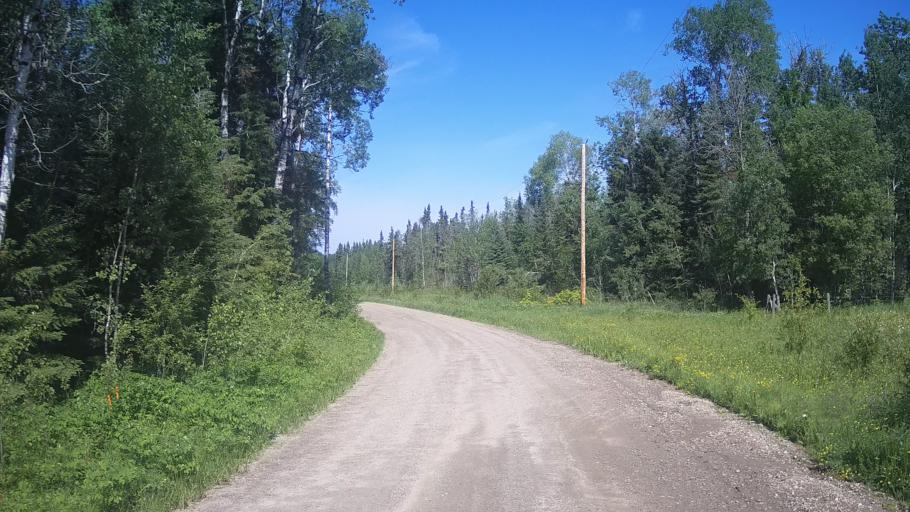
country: CA
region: Ontario
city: Dryden
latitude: 49.8172
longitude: -93.3309
